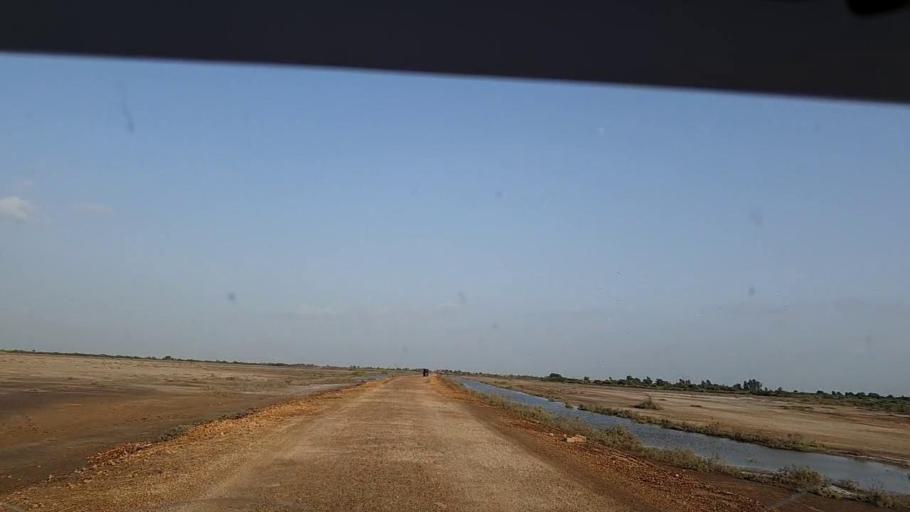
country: PK
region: Sindh
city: Badin
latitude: 24.5502
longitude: 68.8774
